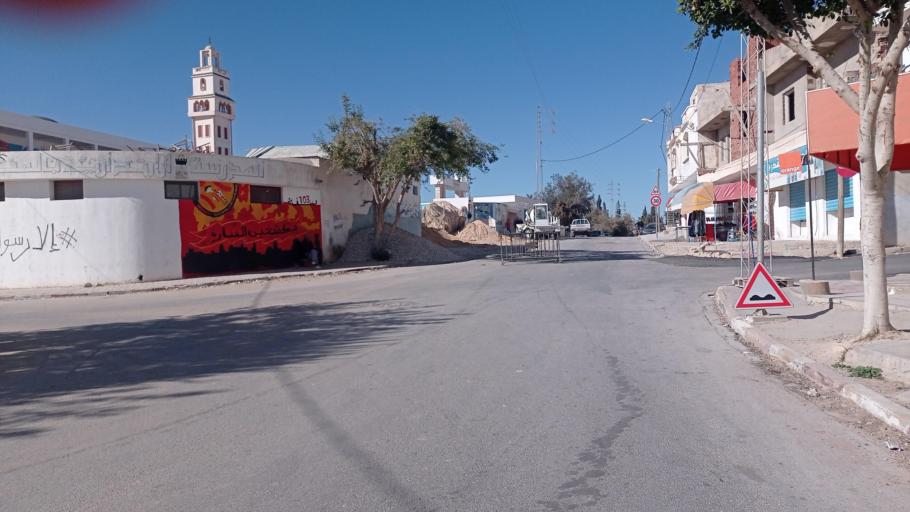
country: TN
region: Qabis
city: Gabes
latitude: 33.8482
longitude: 10.1087
